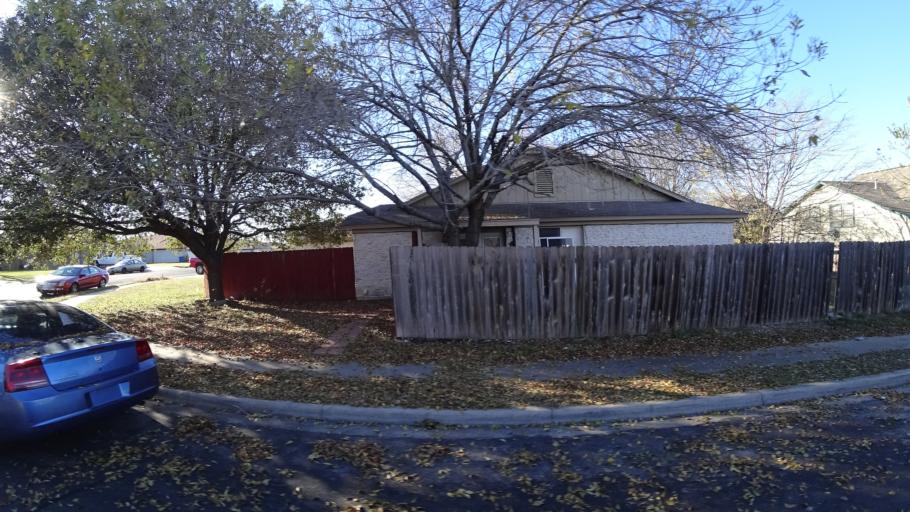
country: US
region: Texas
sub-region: Travis County
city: Wells Branch
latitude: 30.3987
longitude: -97.7022
